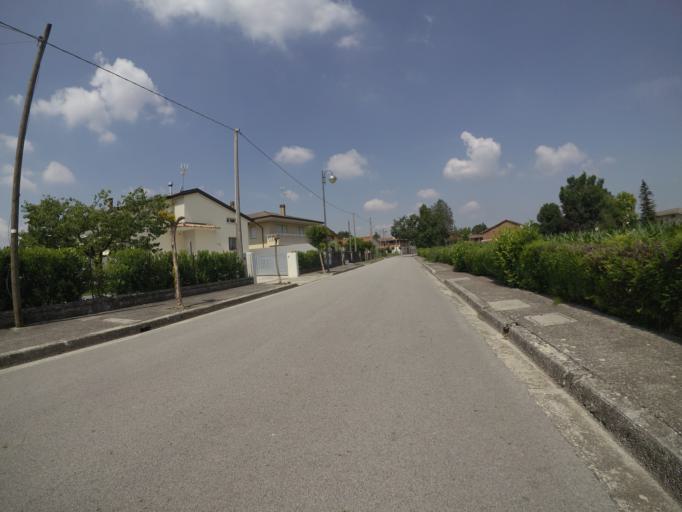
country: IT
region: Friuli Venezia Giulia
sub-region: Provincia di Udine
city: Rivignano
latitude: 45.8843
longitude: 13.0588
